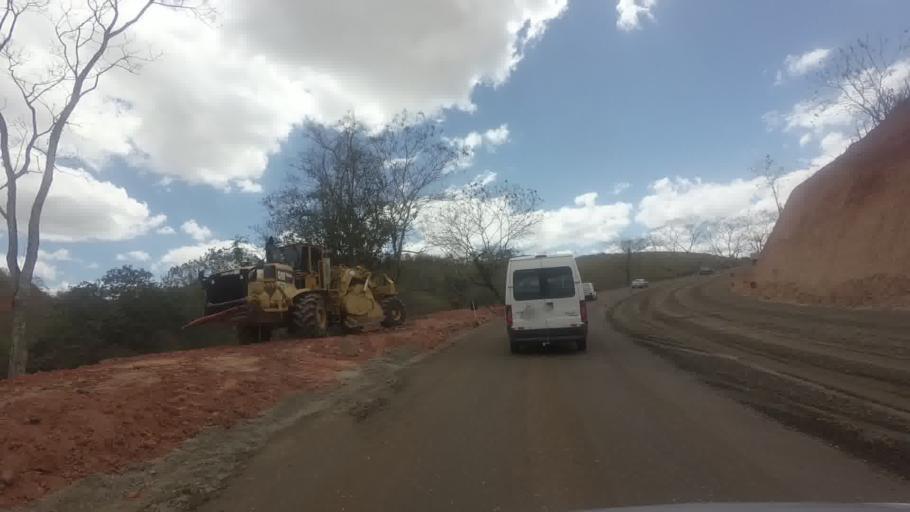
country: BR
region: Rio de Janeiro
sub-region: Santo Antonio De Padua
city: Santo Antonio de Padua
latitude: -21.5116
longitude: -42.0914
